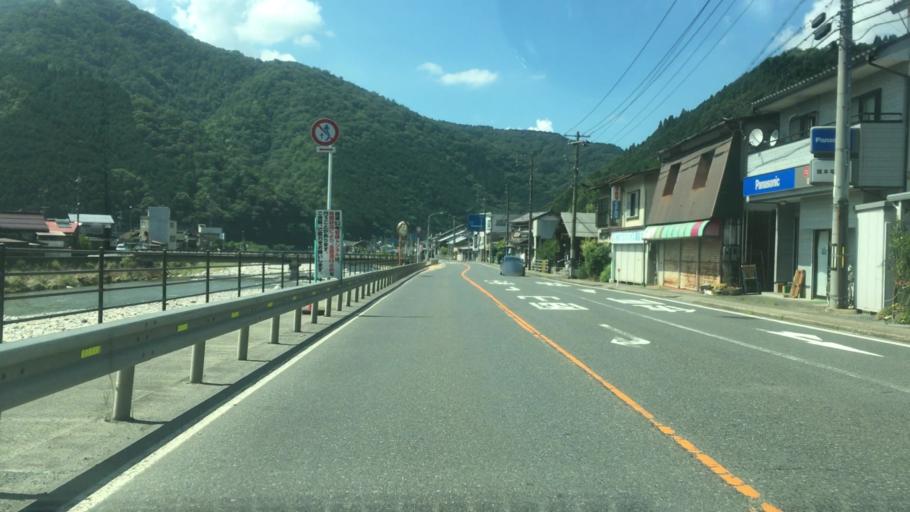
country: JP
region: Tottori
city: Tottori
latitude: 35.2679
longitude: 134.2300
